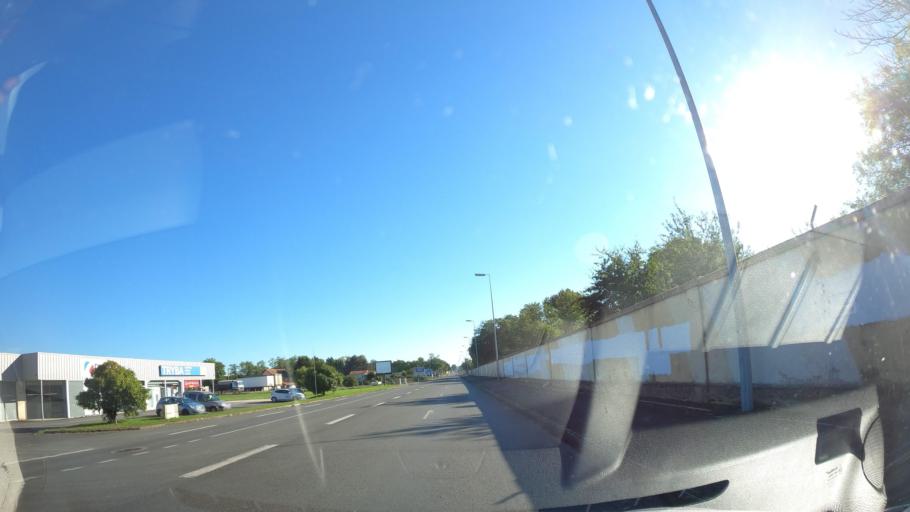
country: FR
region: Aquitaine
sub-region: Departement de la Dordogne
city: Bergerac
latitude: 44.8441
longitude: 0.5034
